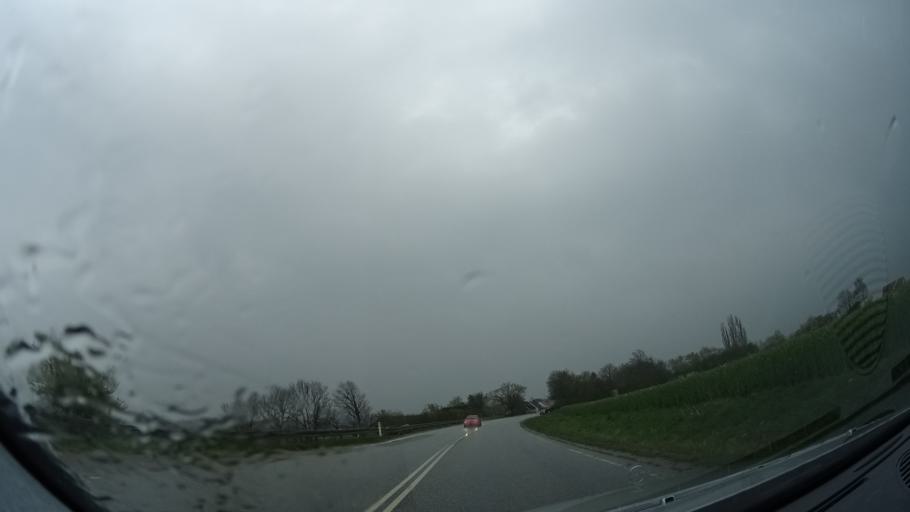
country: DK
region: Zealand
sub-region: Odsherred Kommune
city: Hojby
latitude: 55.8399
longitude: 11.5729
